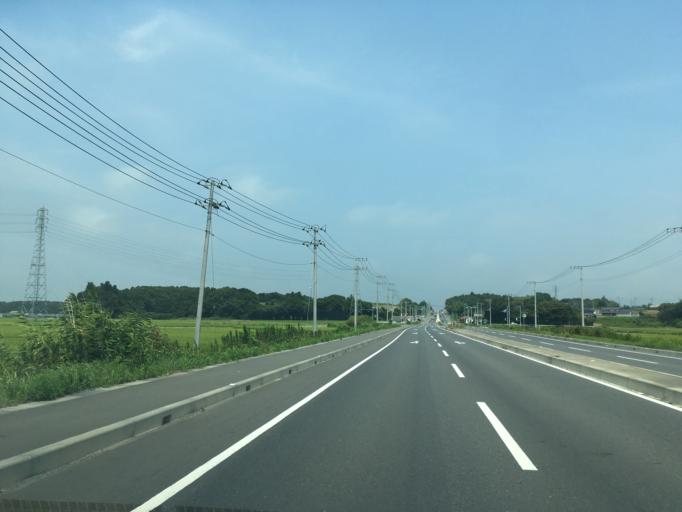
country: JP
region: Ibaraki
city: Oarai
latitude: 36.3596
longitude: 140.5795
